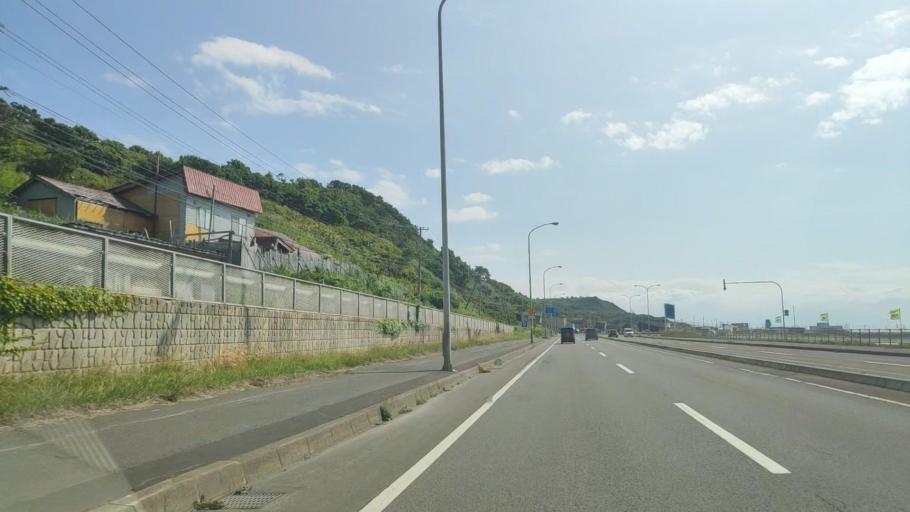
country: JP
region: Hokkaido
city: Rumoi
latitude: 44.0027
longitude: 141.6583
